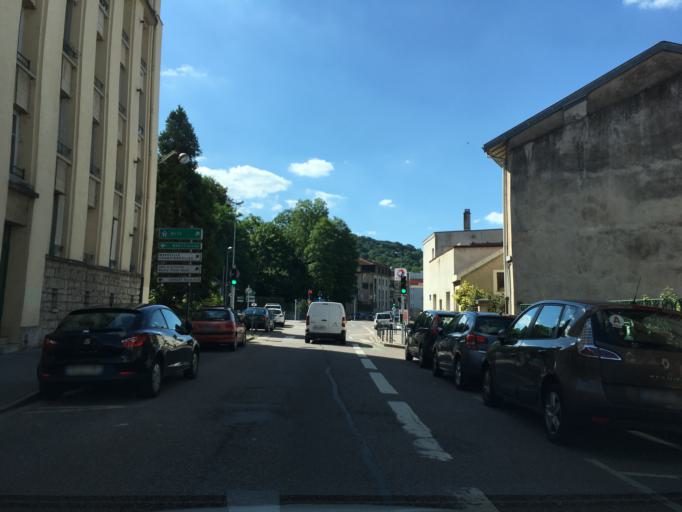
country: FR
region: Lorraine
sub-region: Departement de Meurthe-et-Moselle
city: Maxeville
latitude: 48.7045
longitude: 6.1702
